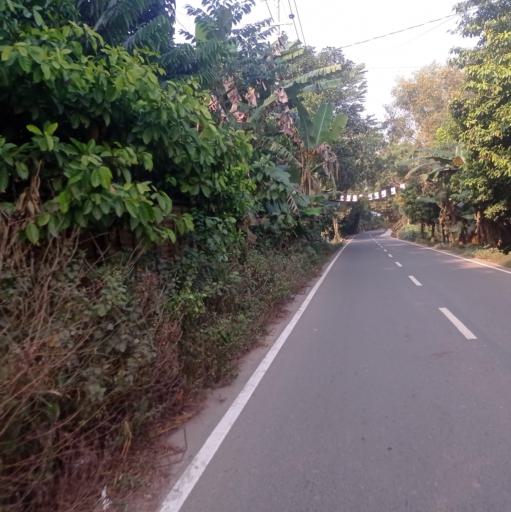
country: BD
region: Dhaka
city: Bhairab Bazar
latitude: 24.0465
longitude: 90.8348
